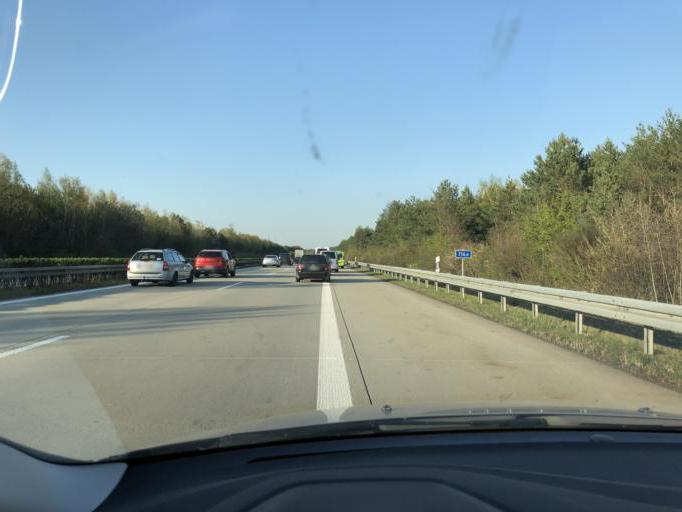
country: DE
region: Brandenburg
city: Ruhland
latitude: 51.4342
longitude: 13.8270
